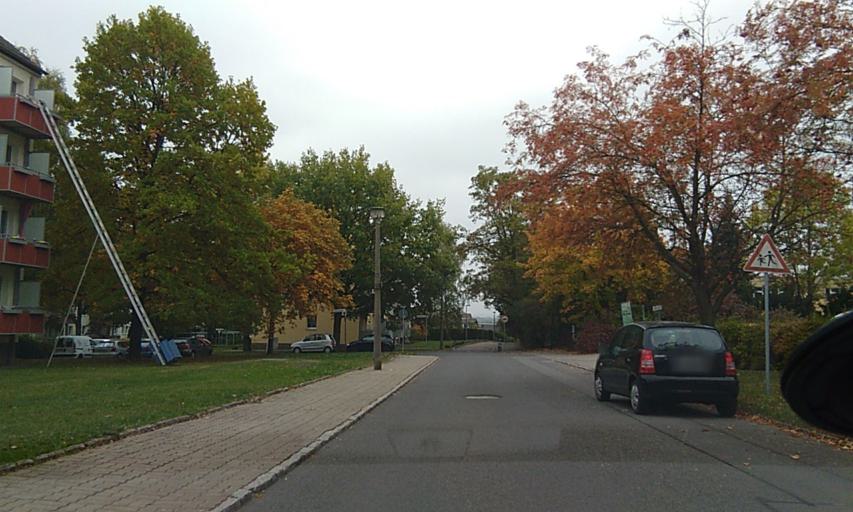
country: DE
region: Saxony
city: Wittgensdorf
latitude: 50.8410
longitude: 12.8705
